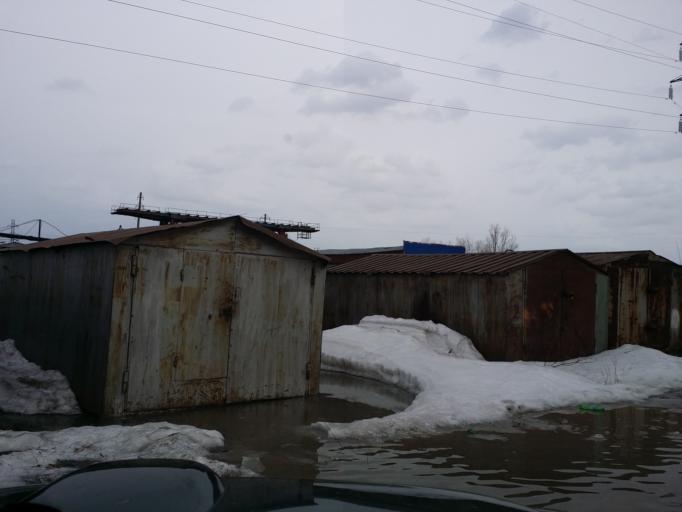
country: RU
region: Khanty-Mansiyskiy Avtonomnyy Okrug
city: Nizhnevartovsk
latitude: 60.9494
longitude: 76.5430
